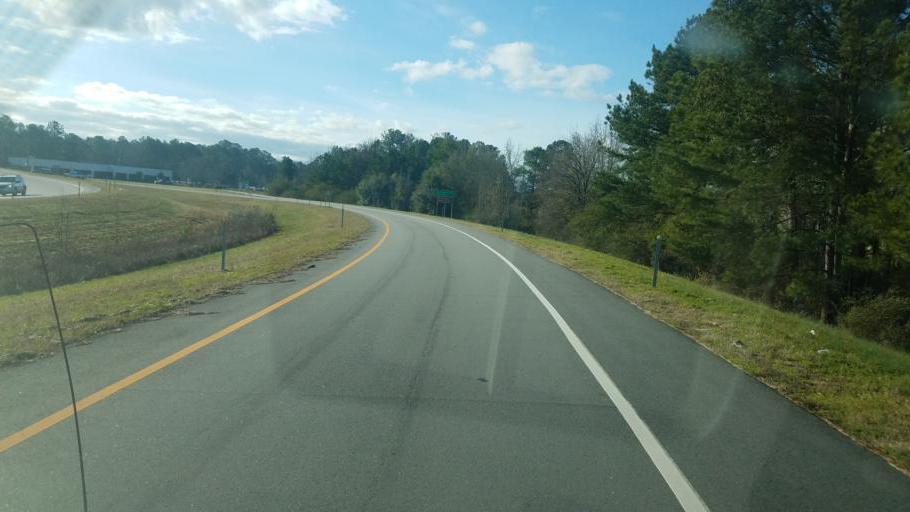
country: US
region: South Carolina
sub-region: Richland County
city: Dentsville
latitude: 34.1007
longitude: -80.9611
